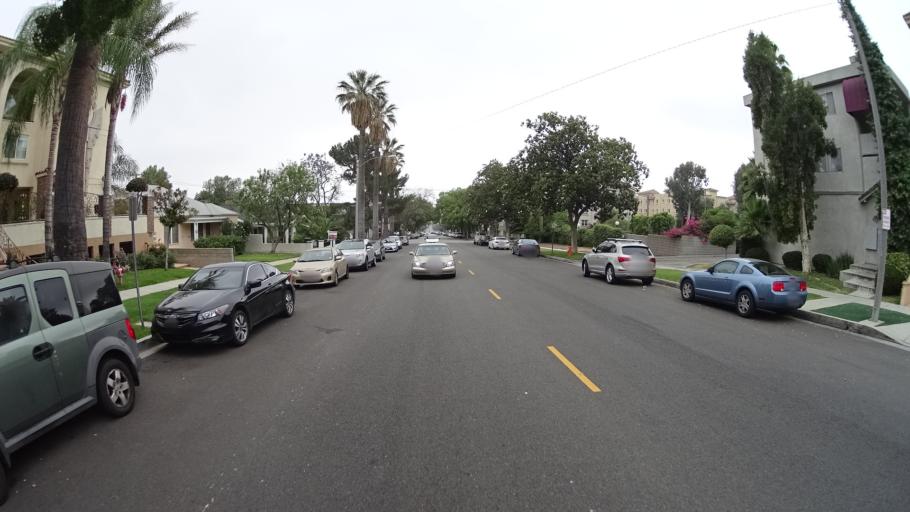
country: US
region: California
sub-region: Los Angeles County
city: Burbank
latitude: 34.1842
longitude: -118.3034
